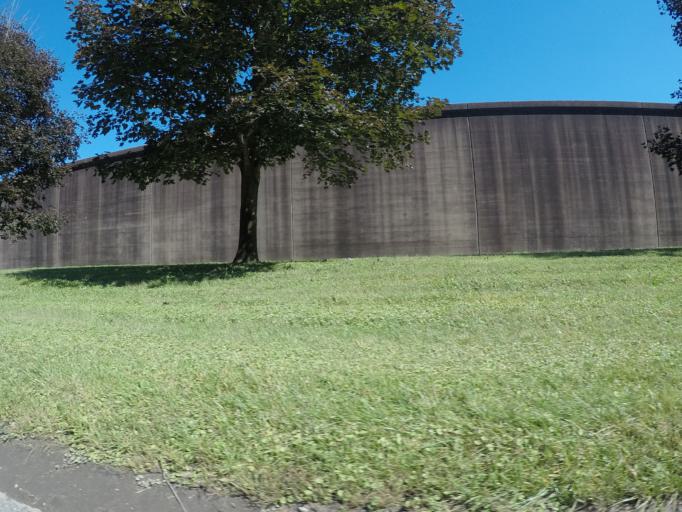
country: US
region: West Virginia
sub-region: Cabell County
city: Huntington
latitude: 38.4151
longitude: -82.3882
